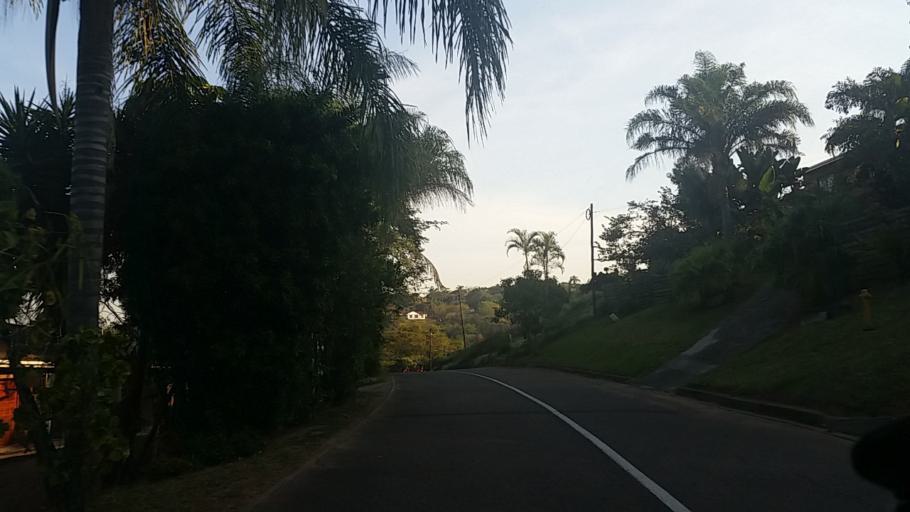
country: ZA
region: KwaZulu-Natal
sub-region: eThekwini Metropolitan Municipality
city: Berea
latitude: -29.8508
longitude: 30.9222
